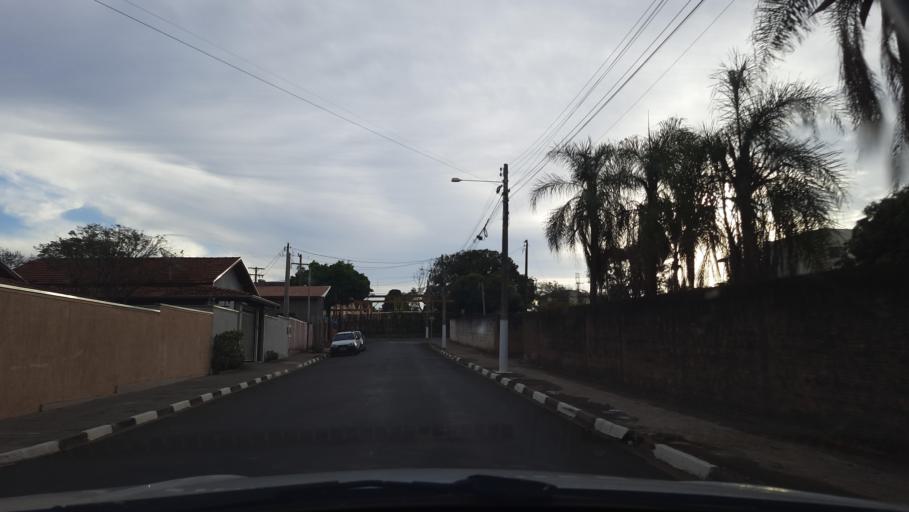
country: BR
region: Sao Paulo
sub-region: Casa Branca
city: Casa Branca
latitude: -21.7805
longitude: -47.0662
